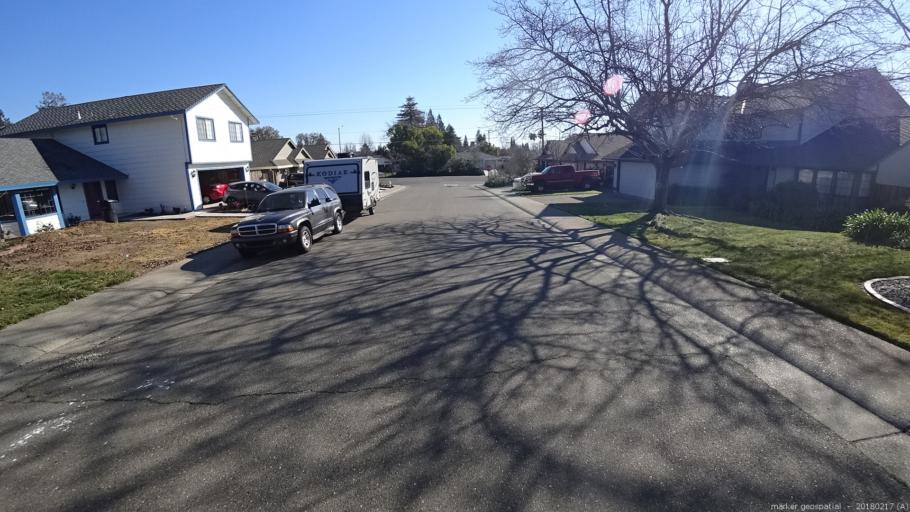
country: US
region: California
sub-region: Sacramento County
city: Orangevale
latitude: 38.6647
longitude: -121.2032
